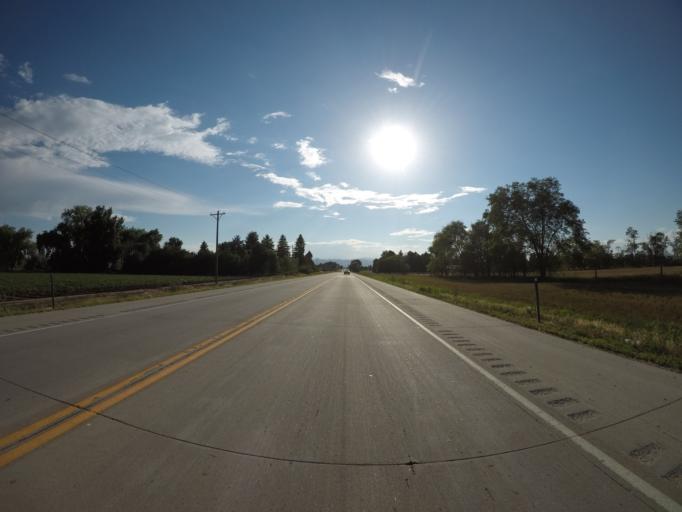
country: US
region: Colorado
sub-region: Weld County
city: Windsor
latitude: 40.5809
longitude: -104.9517
